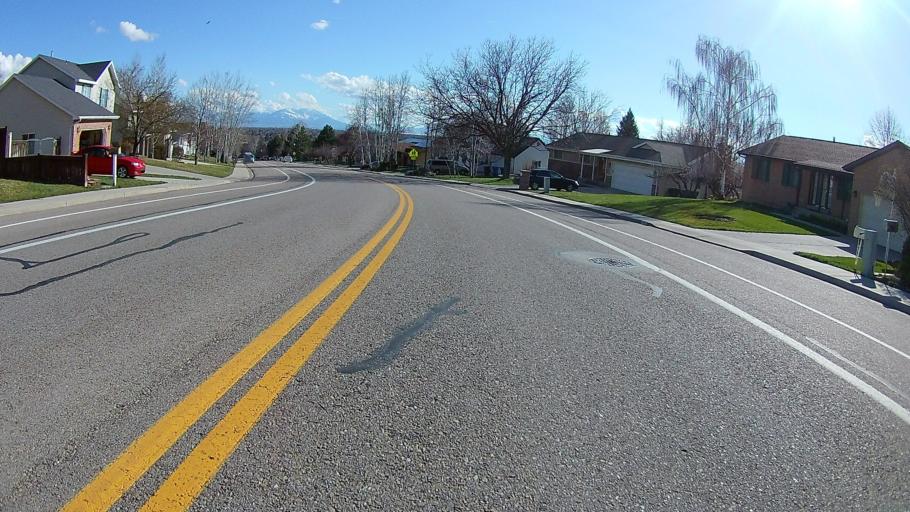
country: US
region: Utah
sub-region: Utah County
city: Lindon
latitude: 40.3317
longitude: -111.6876
